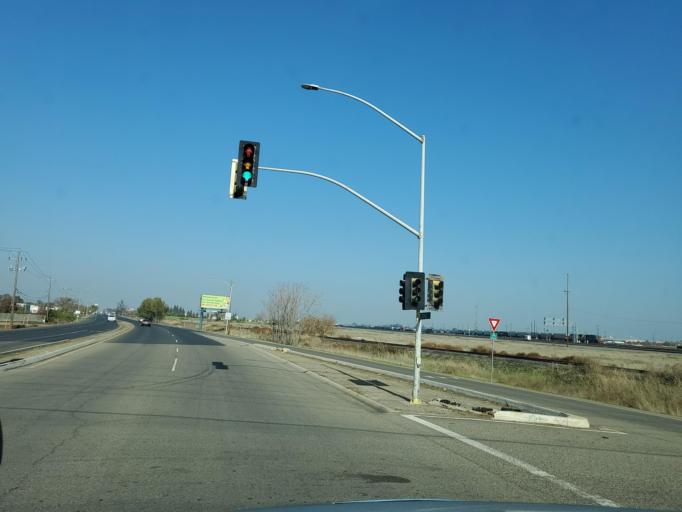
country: US
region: California
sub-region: San Joaquin County
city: Taft Mosswood
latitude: 37.9111
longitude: -121.2757
